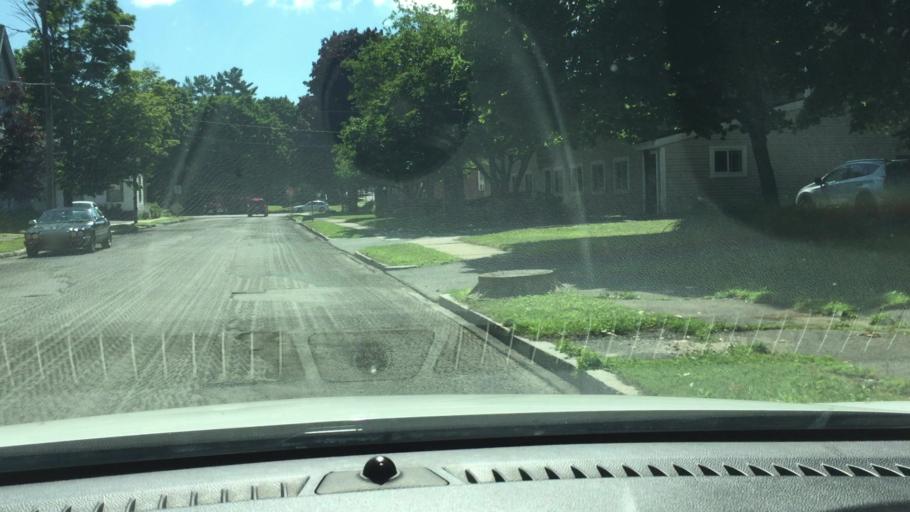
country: US
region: Massachusetts
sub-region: Berkshire County
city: Pittsfield
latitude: 42.4431
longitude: -73.2568
